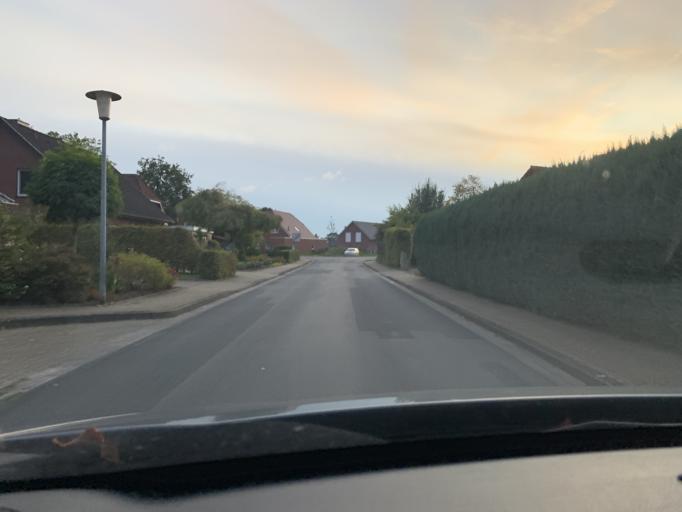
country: DE
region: Lower Saxony
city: Westerstede
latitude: 53.2530
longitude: 7.9052
